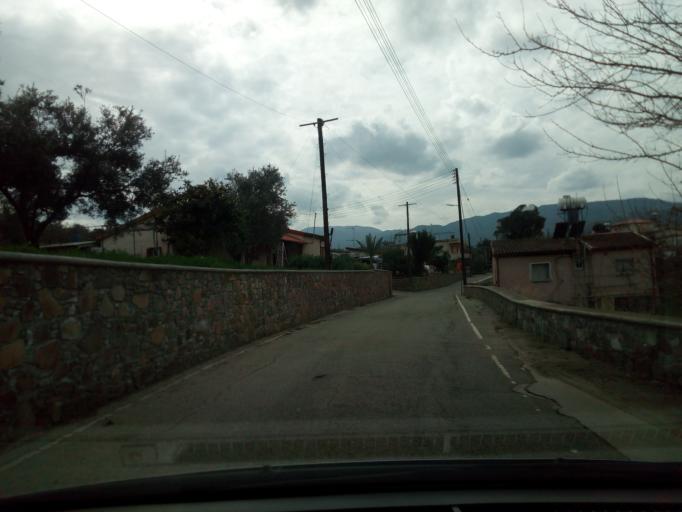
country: CY
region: Lefkosia
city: Lefka
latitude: 35.0712
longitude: 32.8910
